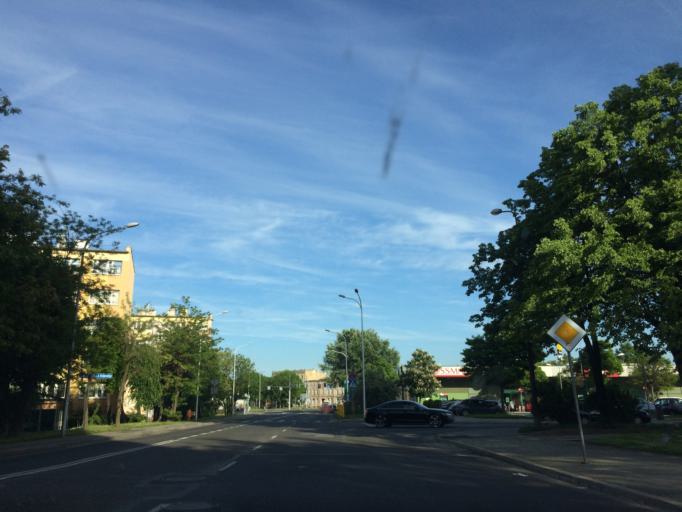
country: PL
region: Lower Silesian Voivodeship
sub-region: Powiat swidnicki
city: Swidnica
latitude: 50.8458
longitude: 16.4691
